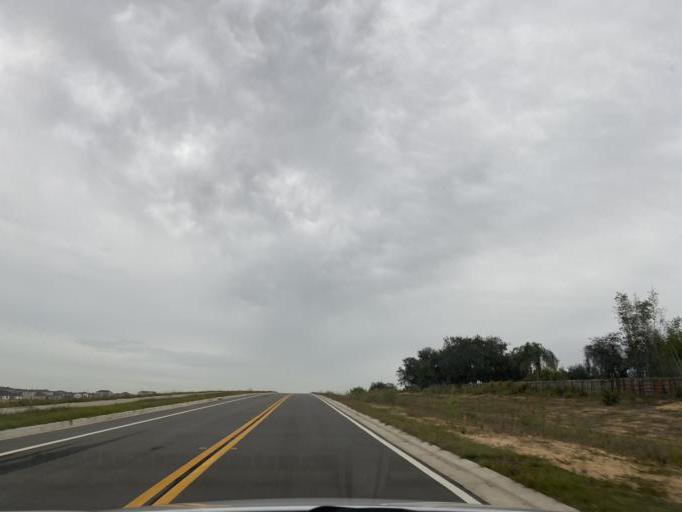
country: US
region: Florida
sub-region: Orange County
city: Oakland
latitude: 28.5330
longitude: -81.6909
